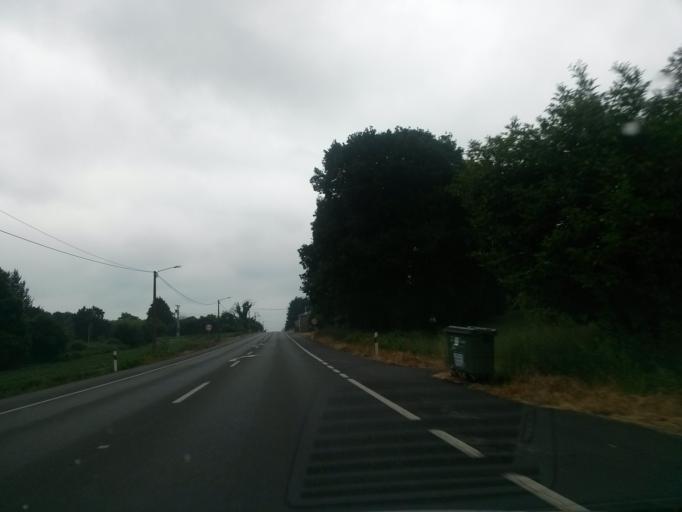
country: ES
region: Galicia
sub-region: Provincia de Lugo
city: Begonte
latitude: 43.1347
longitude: -7.6574
